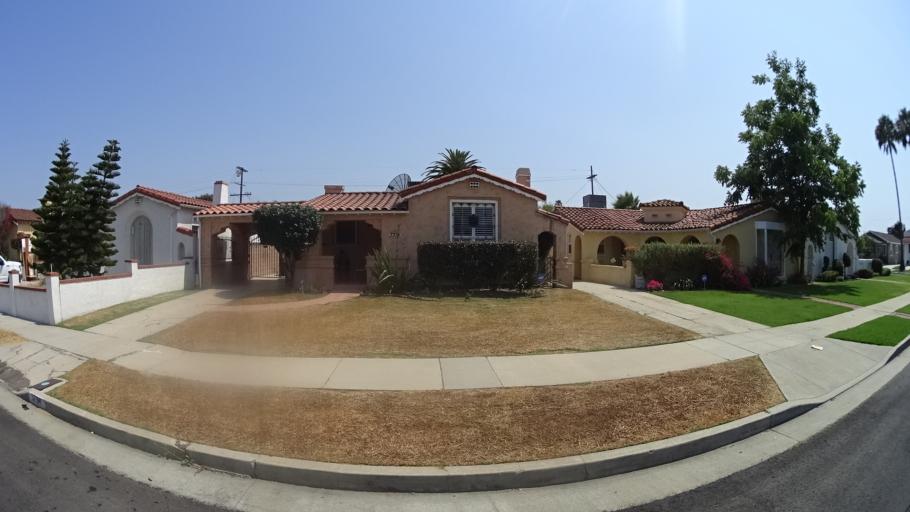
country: US
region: California
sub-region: Los Angeles County
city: View Park-Windsor Hills
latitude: 33.9835
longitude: -118.3382
